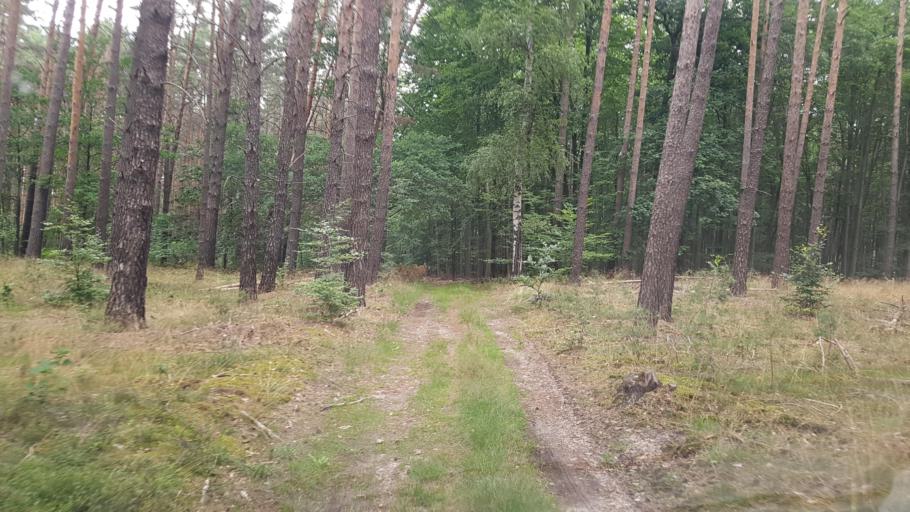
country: DE
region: Brandenburg
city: Crinitz
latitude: 51.7311
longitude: 13.7419
